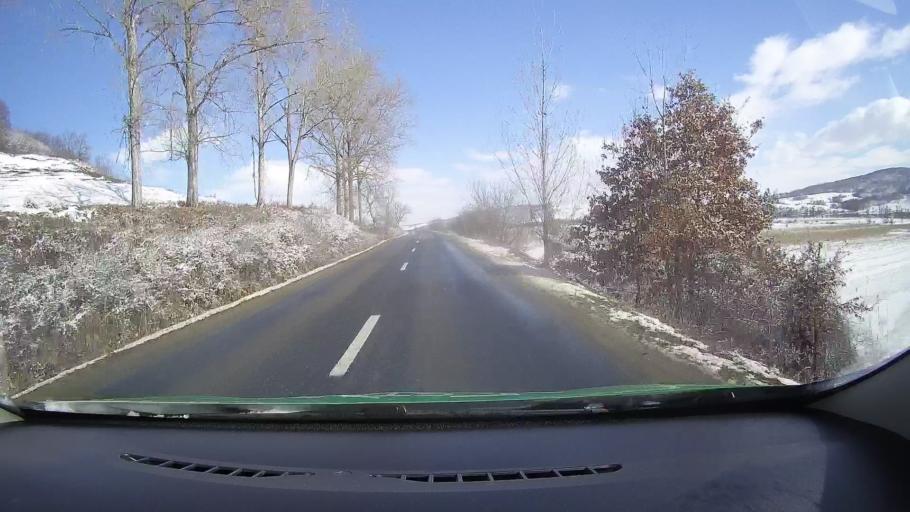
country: RO
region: Sibiu
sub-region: Comuna Nocrich
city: Nocrich
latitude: 45.8459
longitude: 24.4312
